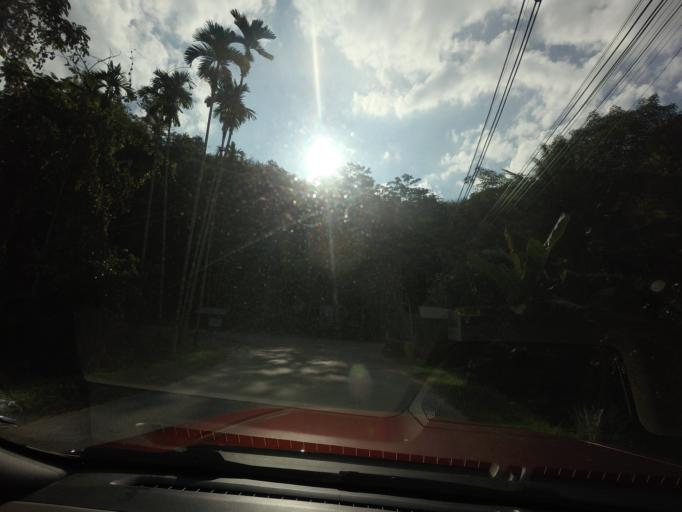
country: TH
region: Yala
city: Than To
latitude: 6.1412
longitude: 101.2975
